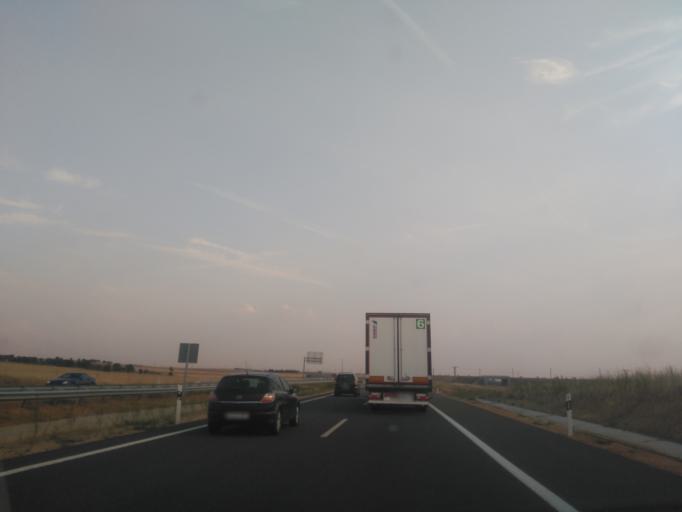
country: ES
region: Castille and Leon
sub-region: Provincia de Zamora
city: Montamarta
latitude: 41.6806
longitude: -5.8055
